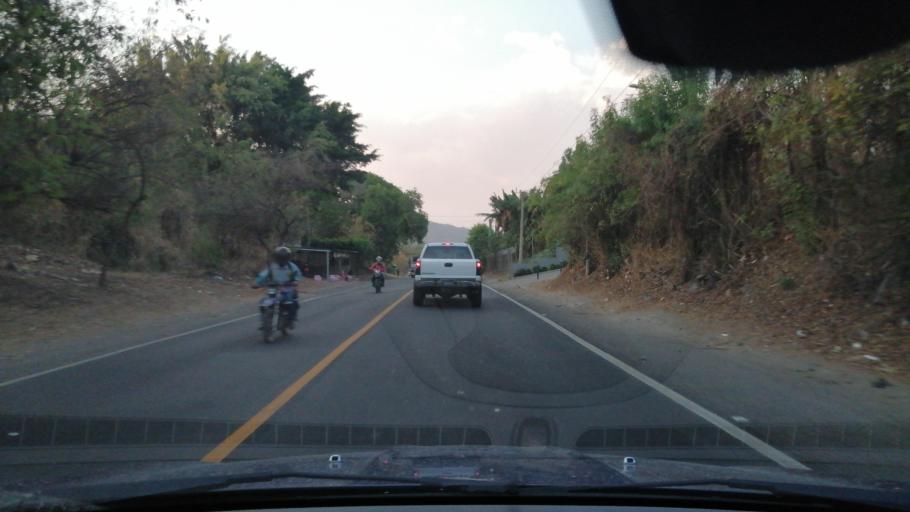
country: SV
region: Santa Ana
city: Santa Ana
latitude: 14.0012
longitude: -89.5416
